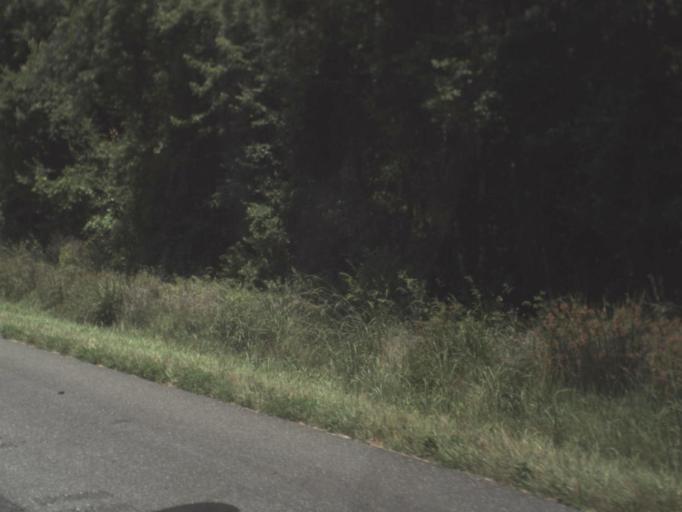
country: US
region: Florida
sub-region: Baker County
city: Macclenny
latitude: 30.2538
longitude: -82.2027
